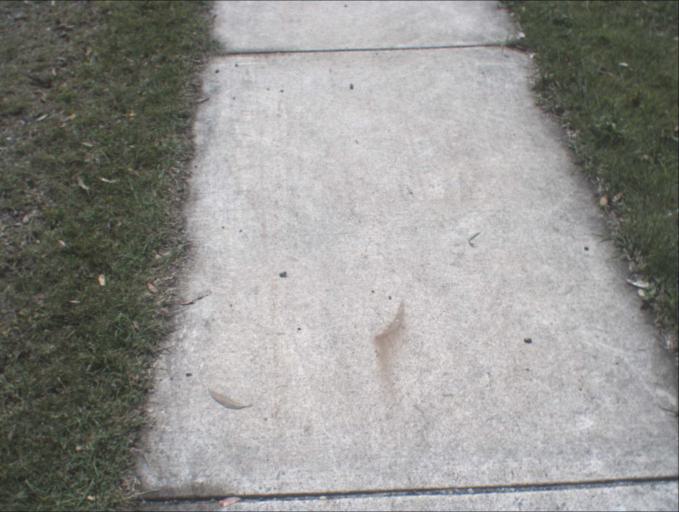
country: AU
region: Queensland
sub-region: Logan
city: North Maclean
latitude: -27.7508
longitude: 153.0142
